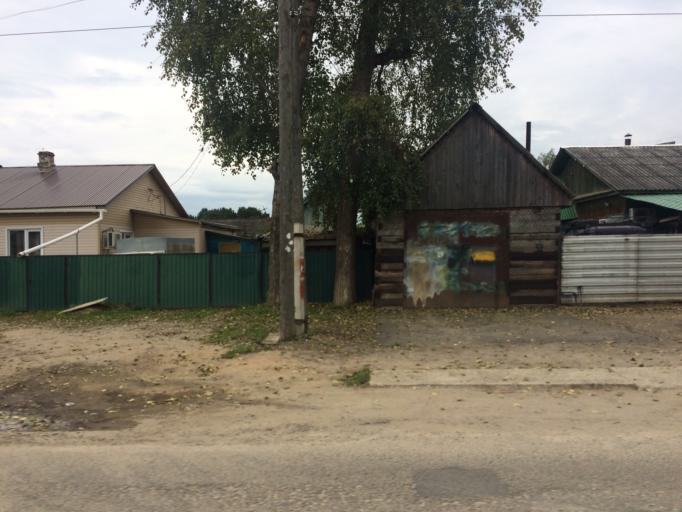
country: RU
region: Primorskiy
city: Dal'nerechensk
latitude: 45.9302
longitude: 133.7612
